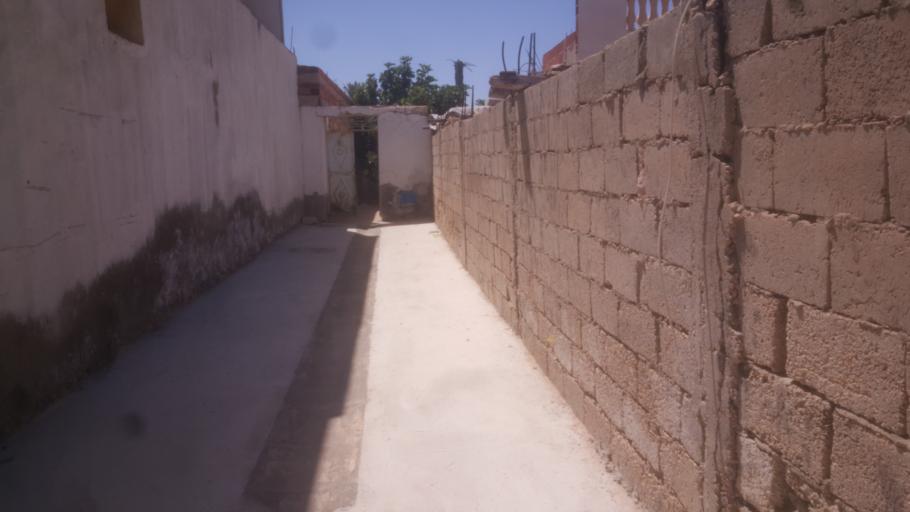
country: TN
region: Qabis
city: Gabes
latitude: 33.9433
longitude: 10.0713
